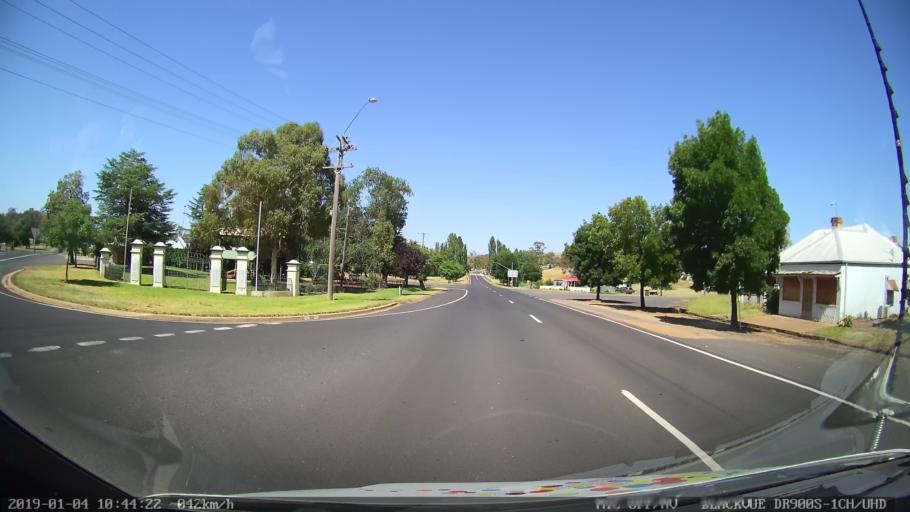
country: AU
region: New South Wales
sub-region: Cabonne
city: Molong
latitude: -33.2874
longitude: 148.7374
